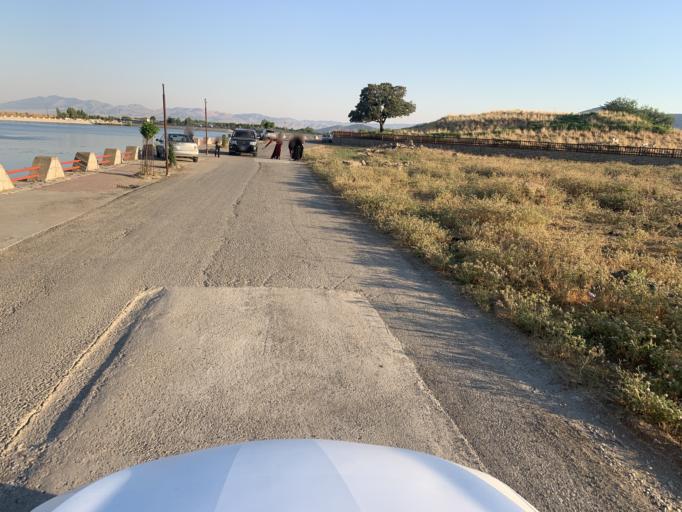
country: IQ
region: As Sulaymaniyah
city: Raniye
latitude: 36.2749
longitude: 44.7537
